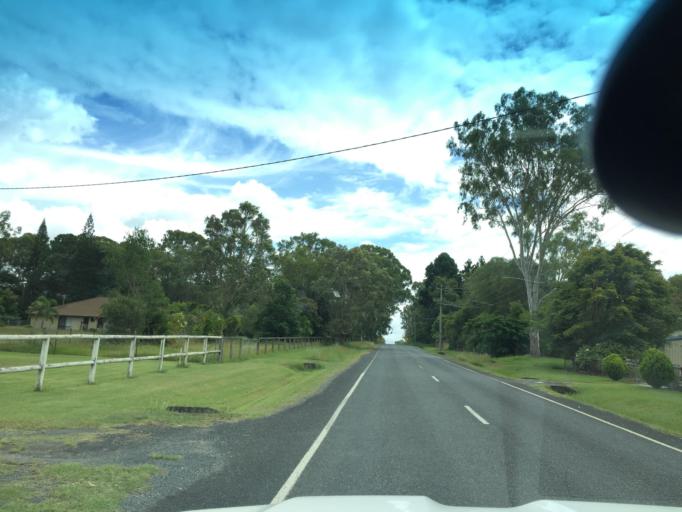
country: AU
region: Queensland
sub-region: Moreton Bay
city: Burpengary
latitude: -27.1680
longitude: 152.9887
